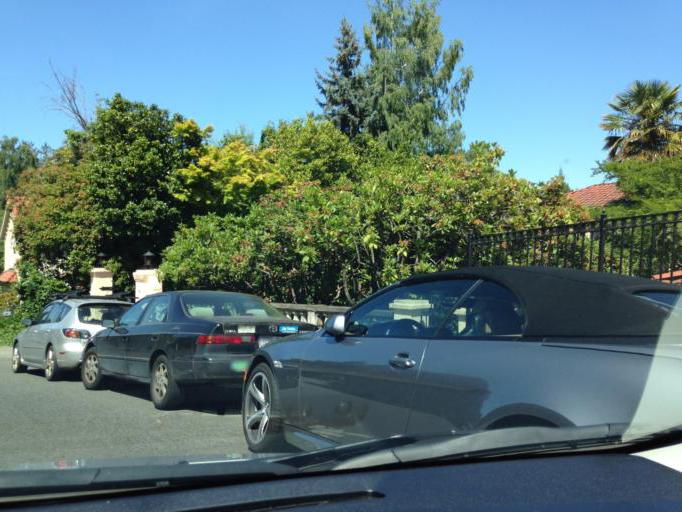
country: US
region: Washington
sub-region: King County
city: Seattle
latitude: 47.6194
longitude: -122.2816
